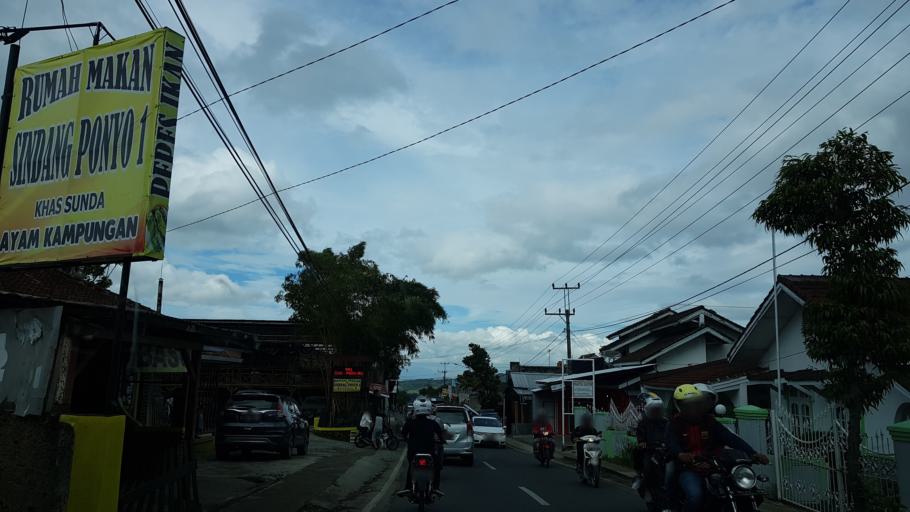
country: ID
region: West Java
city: Banjar
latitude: -7.1090
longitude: 107.4532
